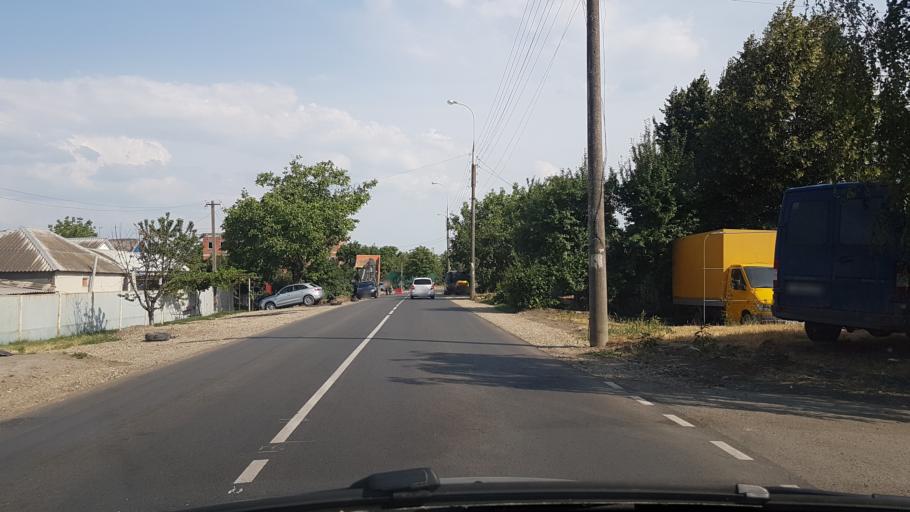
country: RU
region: Krasnodarskiy
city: Pashkovskiy
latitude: 45.0272
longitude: 39.1257
